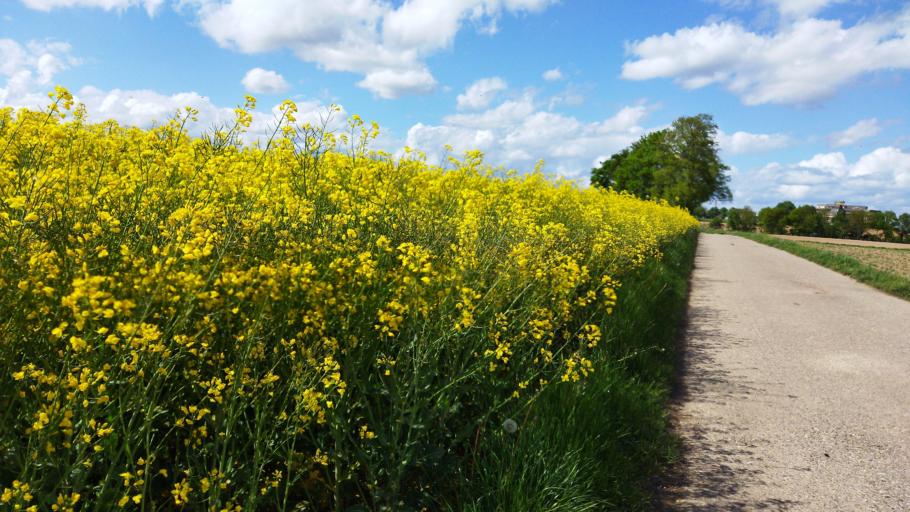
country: DE
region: Baden-Wuerttemberg
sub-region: Regierungsbezirk Stuttgart
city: Bad Rappenau
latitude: 49.2293
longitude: 9.1003
